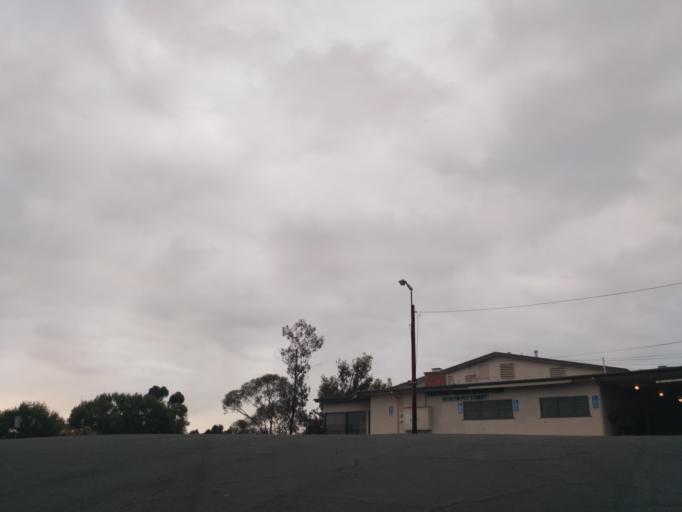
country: US
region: California
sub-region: San Diego County
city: San Diego
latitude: 32.7367
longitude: -117.1651
